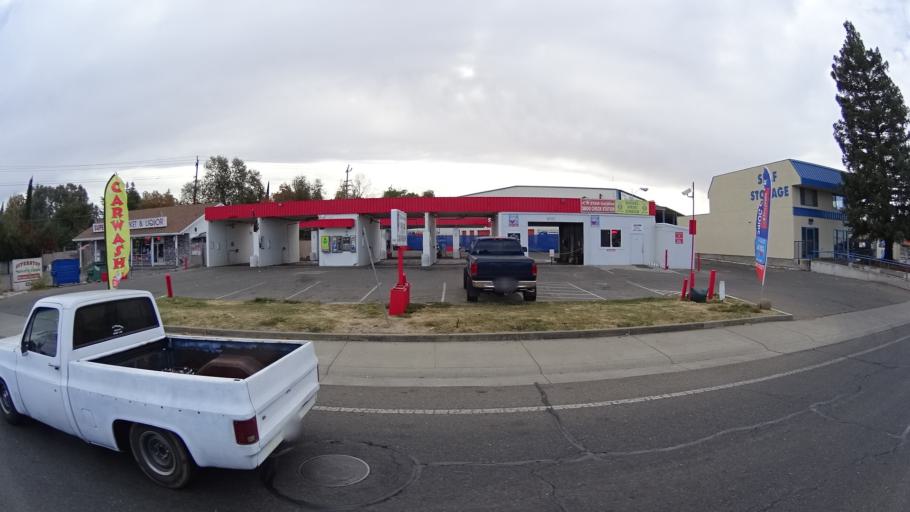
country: US
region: California
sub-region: Sacramento County
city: Antelope
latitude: 38.6802
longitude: -121.3188
